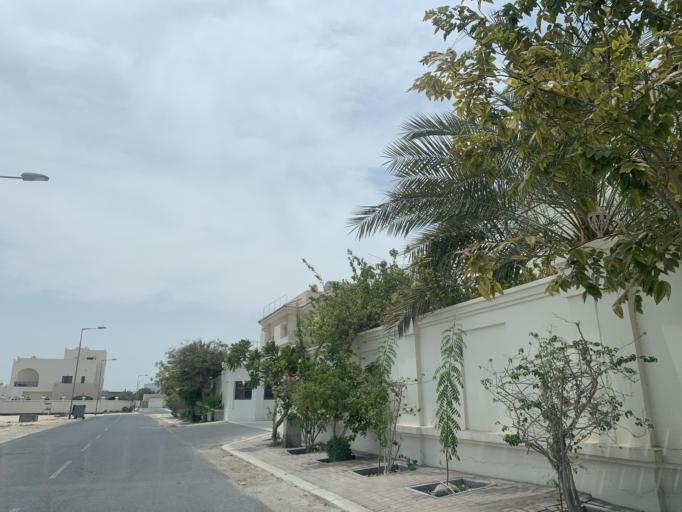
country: BH
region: Northern
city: Madinat `Isa
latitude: 26.1800
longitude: 50.4776
